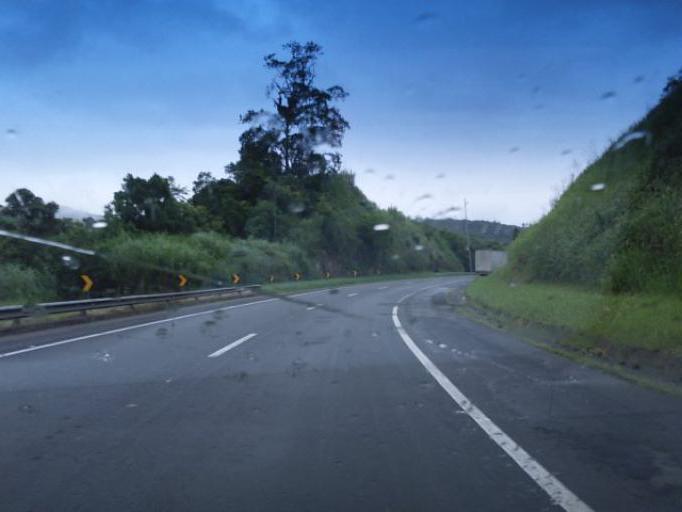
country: BR
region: Sao Paulo
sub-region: Cajati
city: Cajati
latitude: -24.8087
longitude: -48.2131
